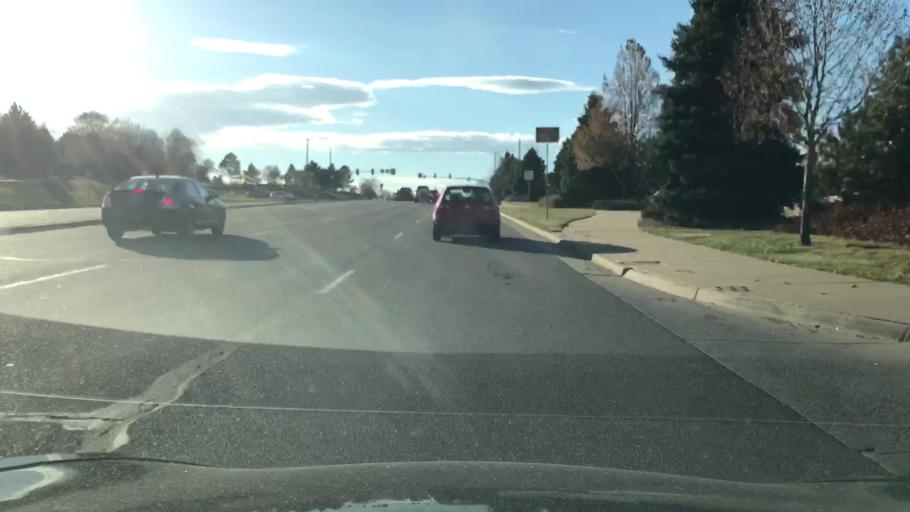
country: US
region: Colorado
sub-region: Adams County
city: Lone Tree
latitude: 39.5364
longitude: -104.8834
